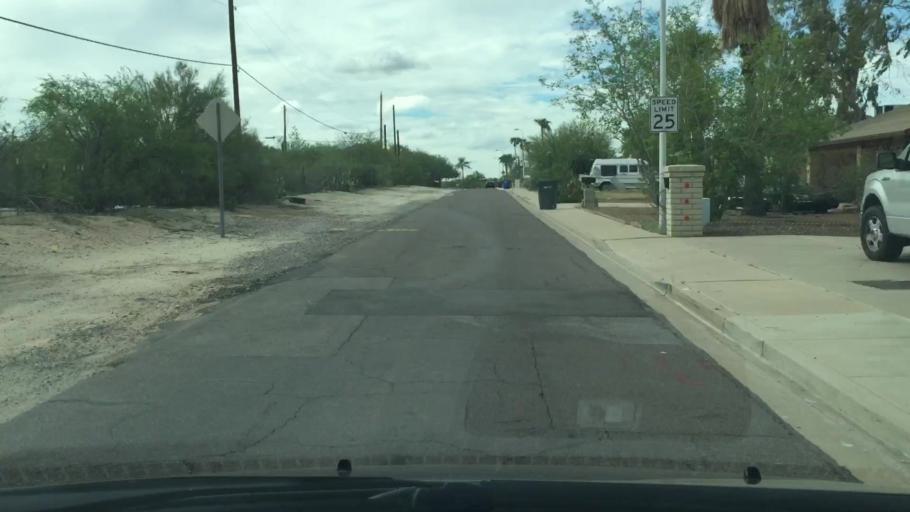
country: US
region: Arizona
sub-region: Maricopa County
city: Guadalupe
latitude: 33.3669
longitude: -112.0410
